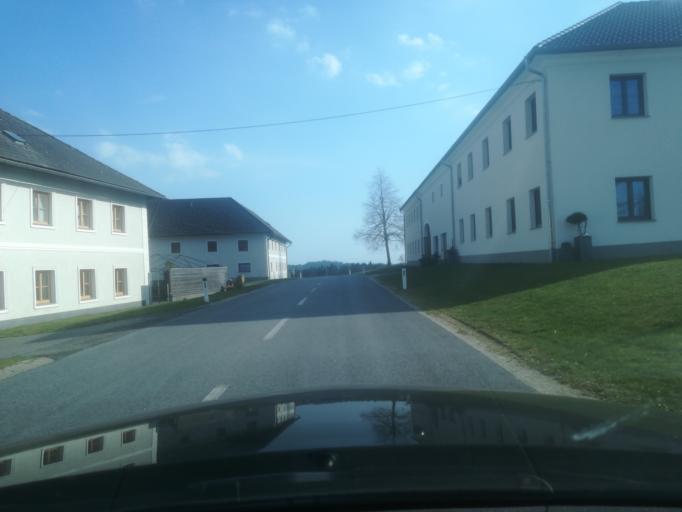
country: AT
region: Upper Austria
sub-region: Politischer Bezirk Perg
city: Perg
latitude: 48.3681
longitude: 14.6476
